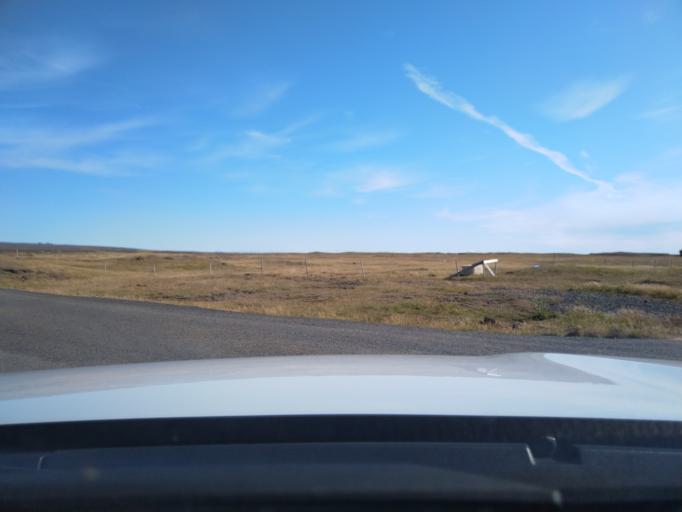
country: IS
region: South
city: THorlakshoefn
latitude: 63.8304
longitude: -21.6765
